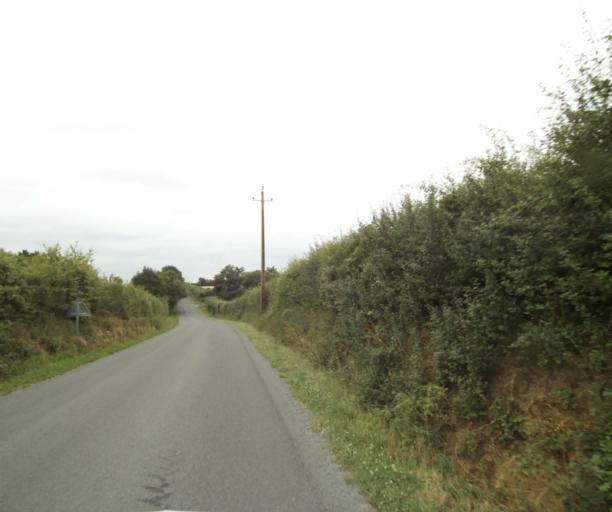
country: FR
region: Pays de la Loire
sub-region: Departement de la Sarthe
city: Sable-sur-Sarthe
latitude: 47.8214
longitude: -0.3336
